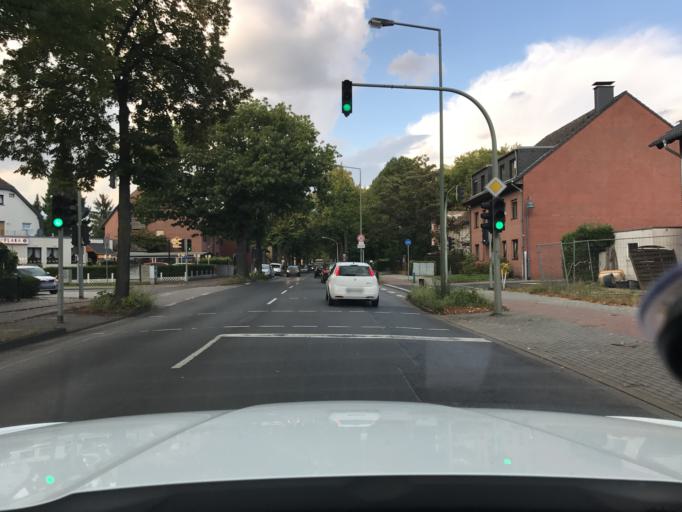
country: DE
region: North Rhine-Westphalia
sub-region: Regierungsbezirk Dusseldorf
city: Hochfeld
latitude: 51.3807
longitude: 6.7692
